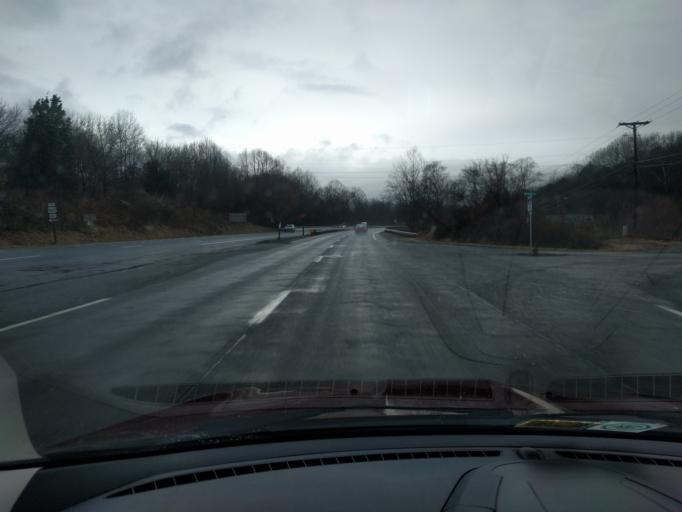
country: US
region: Virginia
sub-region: Giles County
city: Pembroke
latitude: 37.3005
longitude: -80.5573
